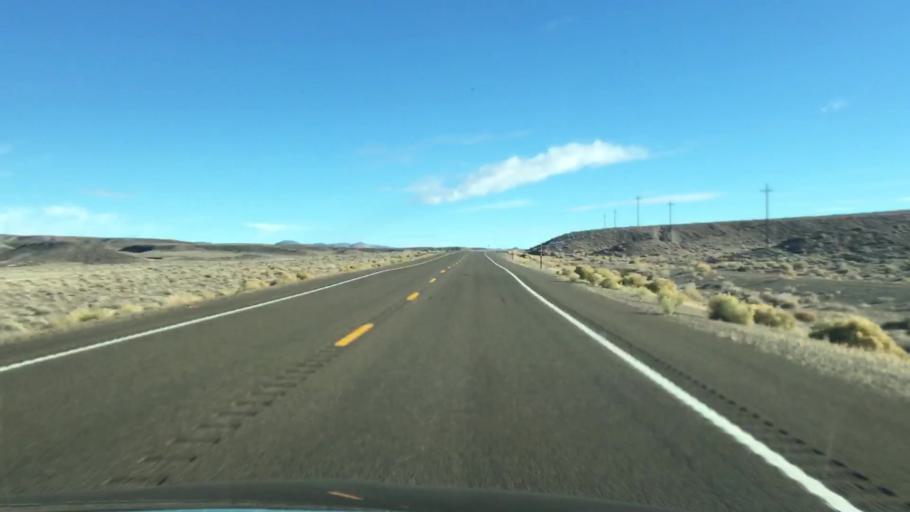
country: US
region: Nevada
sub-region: Mineral County
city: Hawthorne
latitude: 38.2322
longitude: -118.0216
